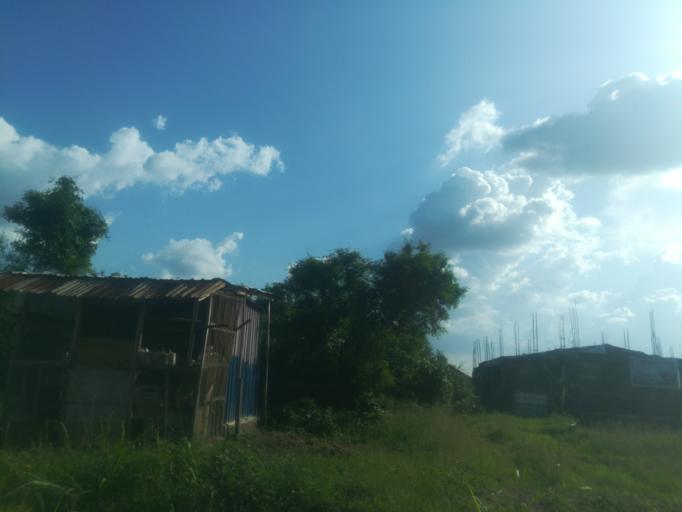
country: NG
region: Oyo
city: Egbeda
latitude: 7.4330
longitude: 3.9786
